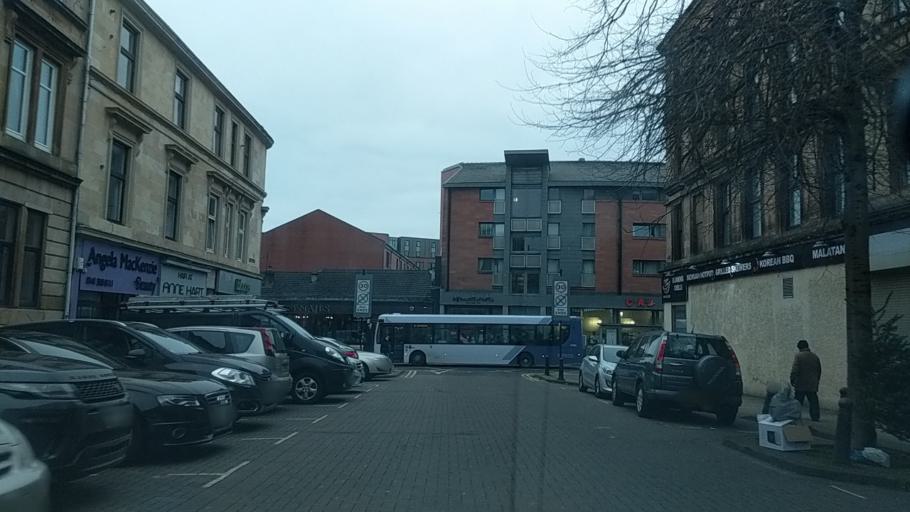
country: GB
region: Scotland
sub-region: Glasgow City
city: Glasgow
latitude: 55.8712
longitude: -4.3006
